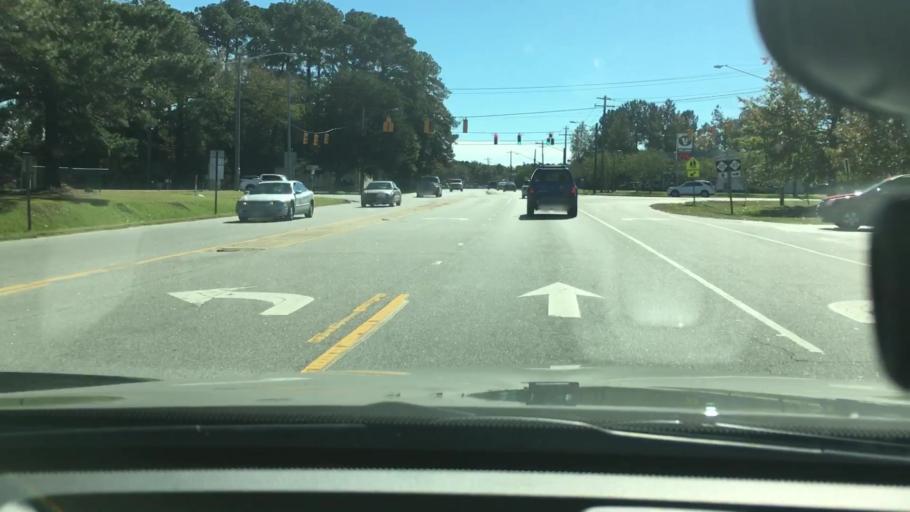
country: US
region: North Carolina
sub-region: Edgecombe County
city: Tarboro
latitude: 35.9004
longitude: -77.5605
